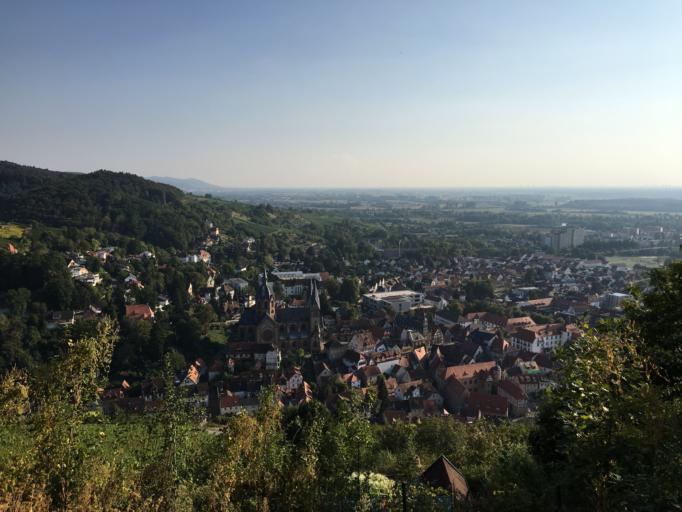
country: DE
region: Hesse
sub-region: Regierungsbezirk Darmstadt
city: Heppenheim an der Bergstrasse
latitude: 49.6446
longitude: 8.6452
